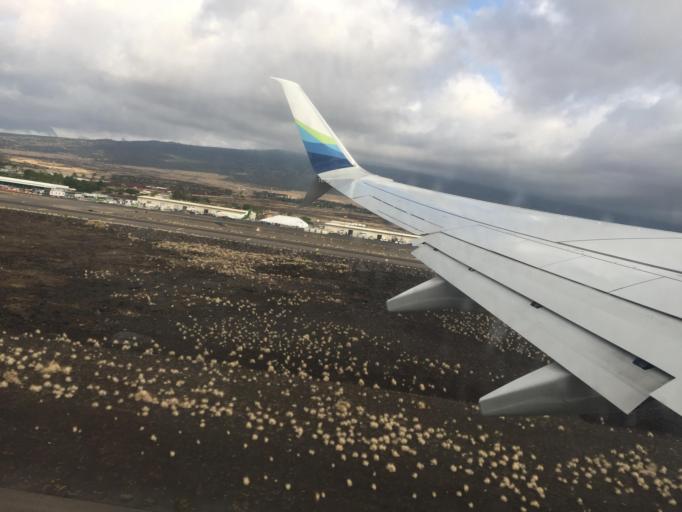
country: US
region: Hawaii
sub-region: Hawaii County
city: Kalaoa
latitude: 19.7308
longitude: -156.0465
